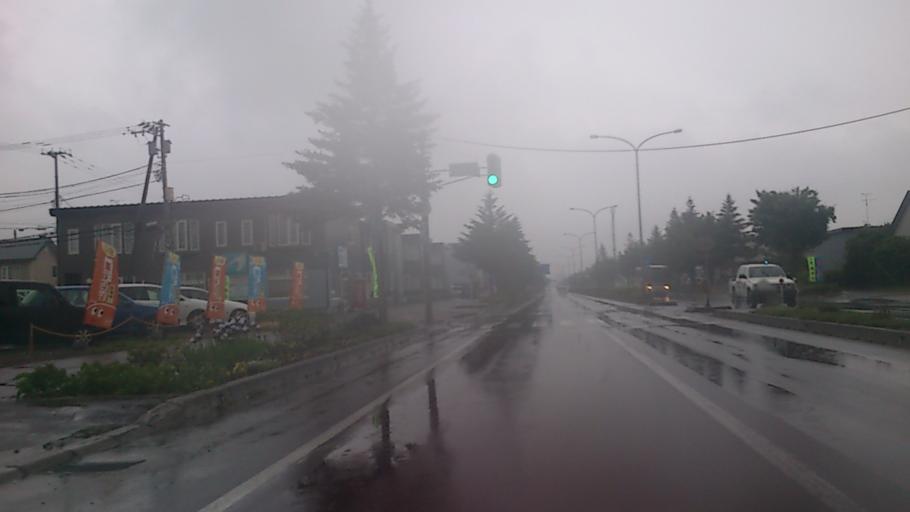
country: JP
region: Hokkaido
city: Obihiro
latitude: 42.9084
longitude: 143.1318
